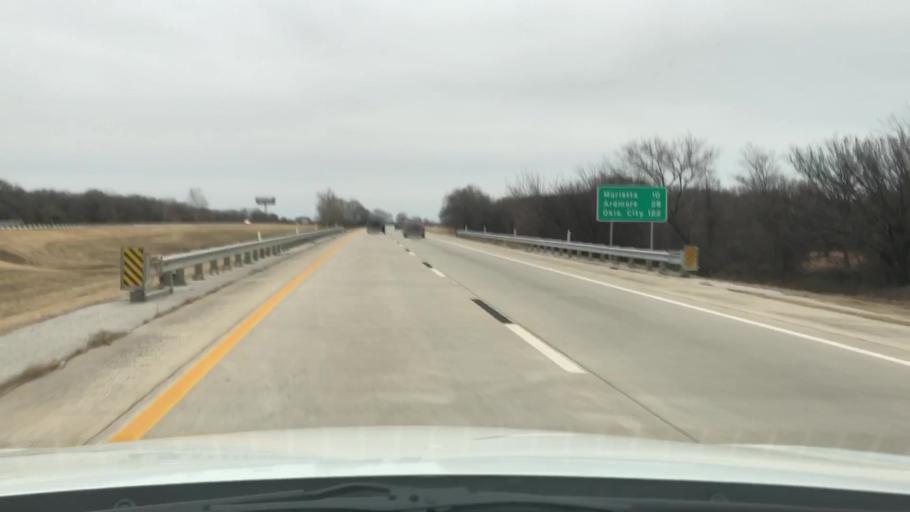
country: US
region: Oklahoma
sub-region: Love County
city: Marietta
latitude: 33.8067
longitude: -97.1344
